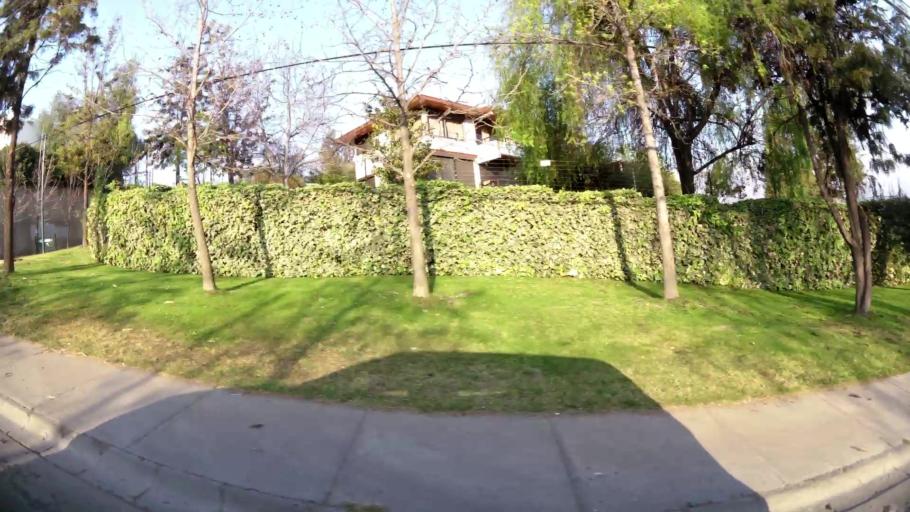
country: CL
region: Santiago Metropolitan
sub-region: Provincia de Santiago
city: Villa Presidente Frei, Nunoa, Santiago, Chile
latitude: -33.3411
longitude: -70.5095
